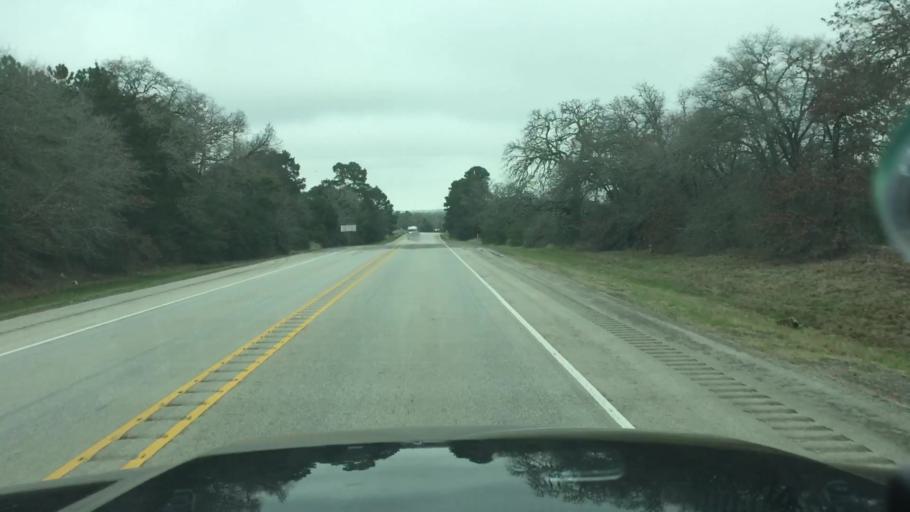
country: US
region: Texas
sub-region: Lee County
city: Giddings
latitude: 30.0774
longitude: -96.9171
